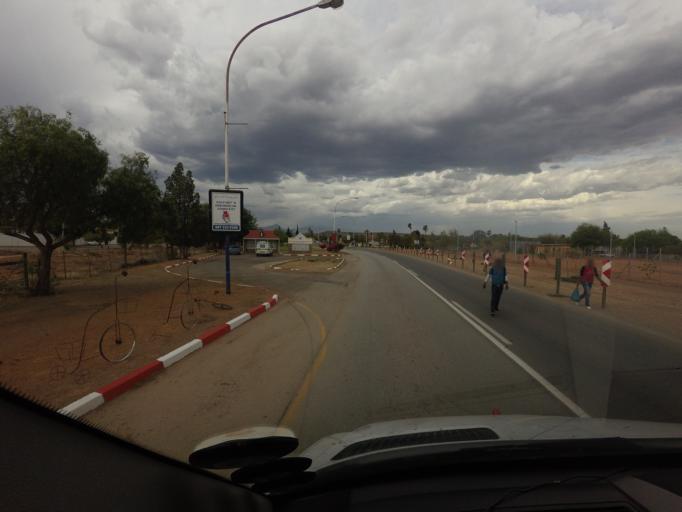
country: ZA
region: Western Cape
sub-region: Eden District Municipality
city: Oudtshoorn
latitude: -33.5929
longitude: 22.1877
